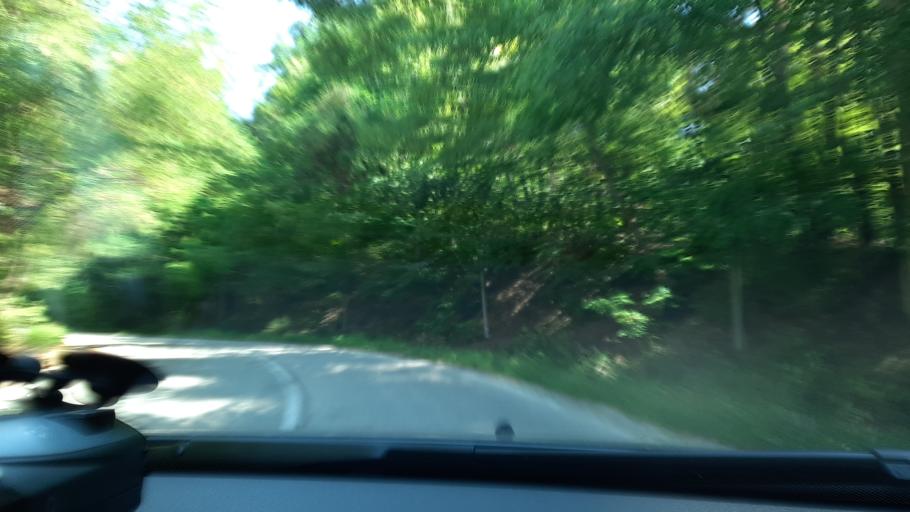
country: RO
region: Gorj
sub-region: Comuna Logresti-Mosteni
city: Logresti Mosteni
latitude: 44.9116
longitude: 23.7648
